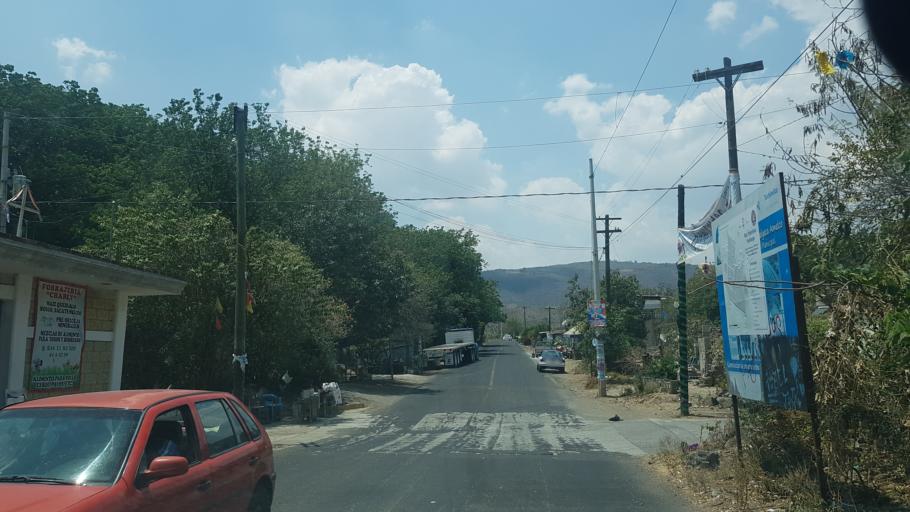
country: MX
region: Puebla
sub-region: Atzitzihuacan
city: Santiago Atzitzihuacan
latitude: 18.8401
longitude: -98.5824
